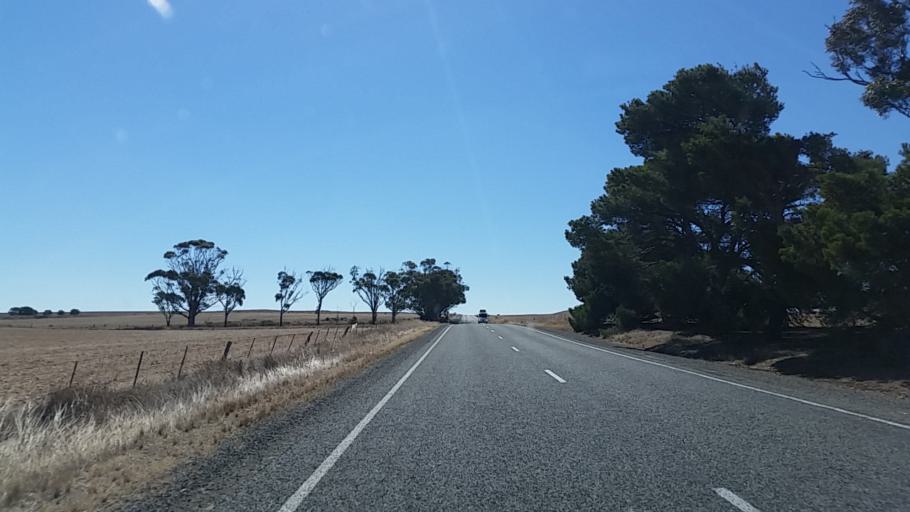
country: AU
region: South Australia
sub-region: Northern Areas
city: Jamestown
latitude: -33.3371
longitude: 138.8924
